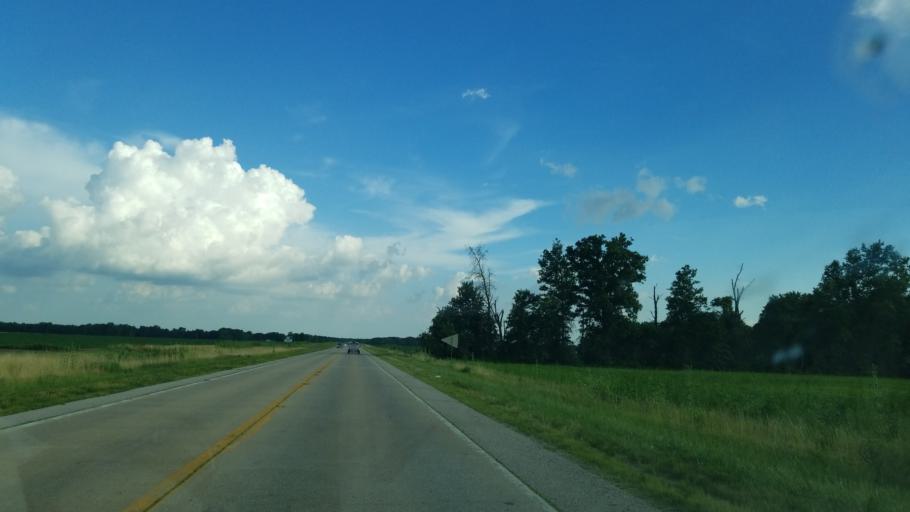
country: US
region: Illinois
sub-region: Marion County
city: Sandoval
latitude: 38.5990
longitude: -89.1084
